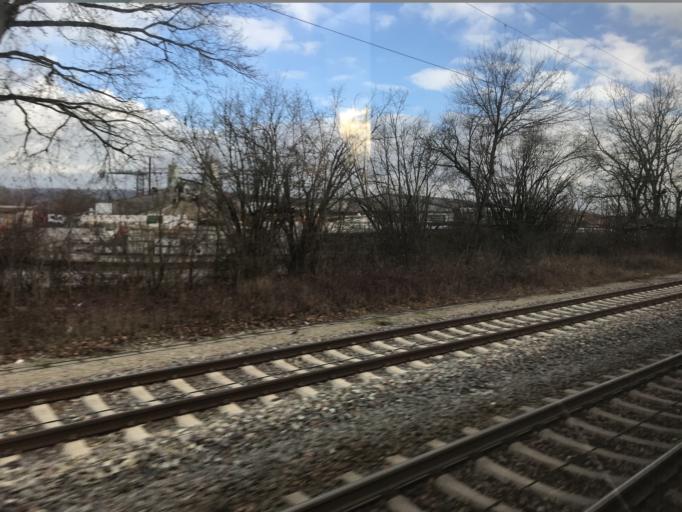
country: DE
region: Baden-Wuerttemberg
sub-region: Freiburg Region
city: Riegel
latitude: 48.1545
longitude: 7.7678
